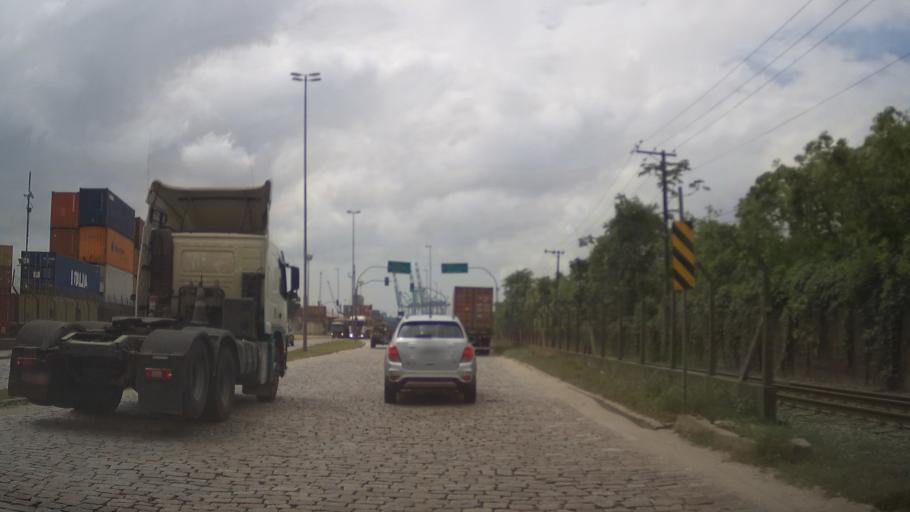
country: BR
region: Sao Paulo
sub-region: Santos
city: Santos
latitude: -23.9270
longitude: -46.3476
